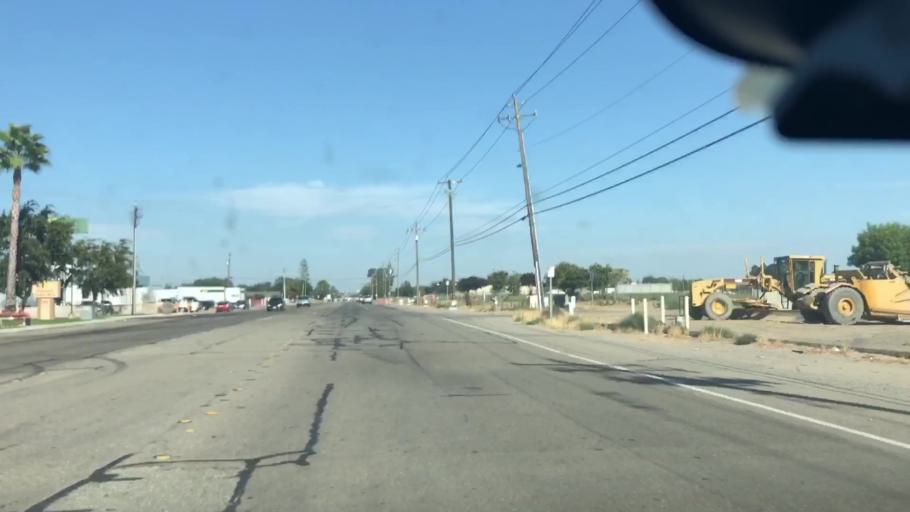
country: US
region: California
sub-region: San Joaquin County
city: Lathrop
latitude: 37.7973
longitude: -121.2613
